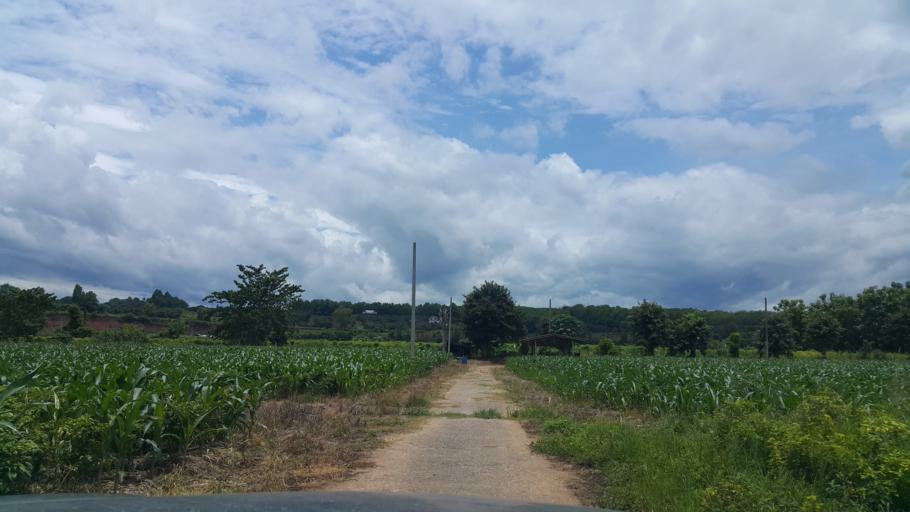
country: TH
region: Chiang Mai
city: Mae Taeng
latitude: 19.1981
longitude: 98.9805
